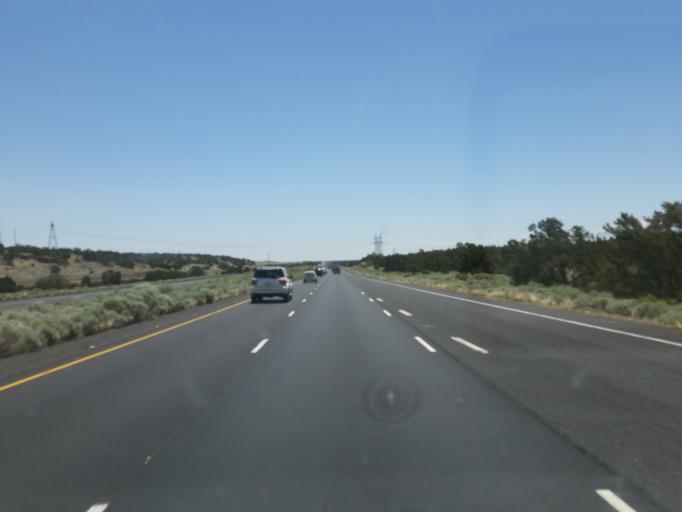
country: US
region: Arizona
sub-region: Coconino County
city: Flagstaff
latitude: 35.1992
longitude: -111.4012
